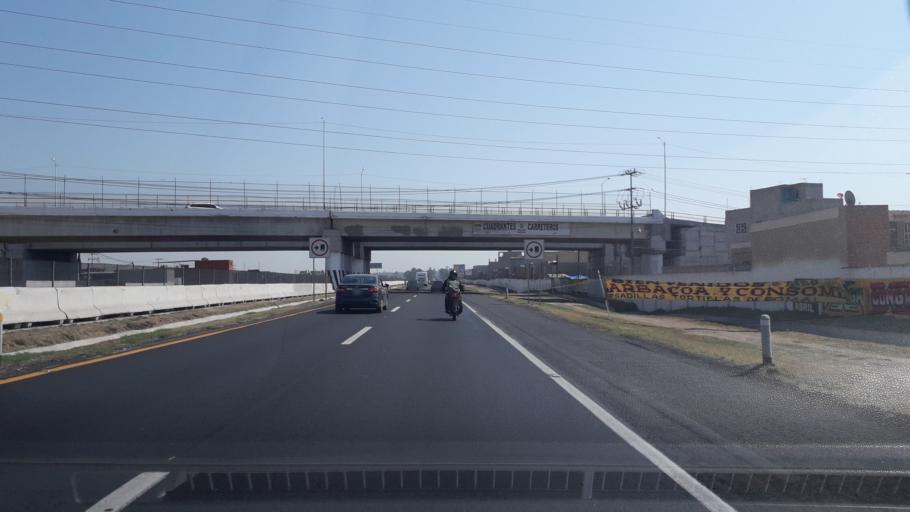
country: MX
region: Mexico
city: Santo Tomas Chiconautla
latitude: 19.6314
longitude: -99.0228
